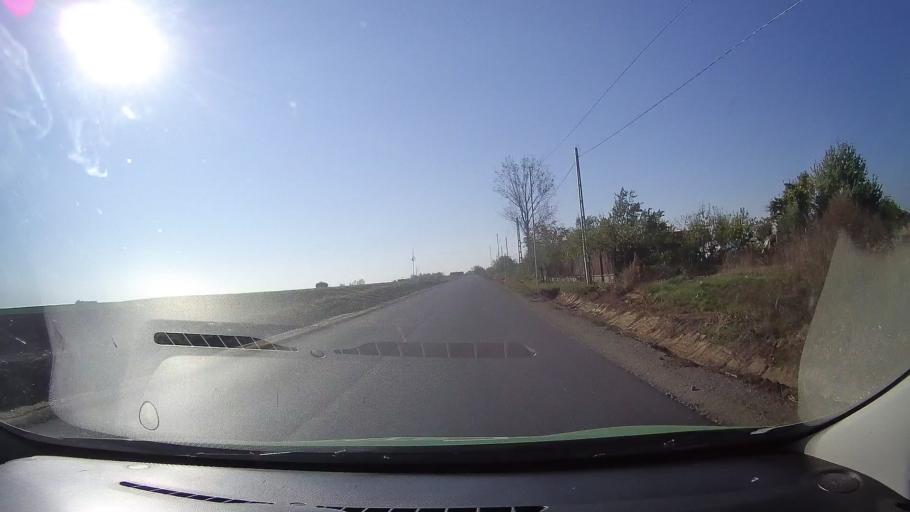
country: RO
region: Satu Mare
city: Carei
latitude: 47.6620
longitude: 22.4603
